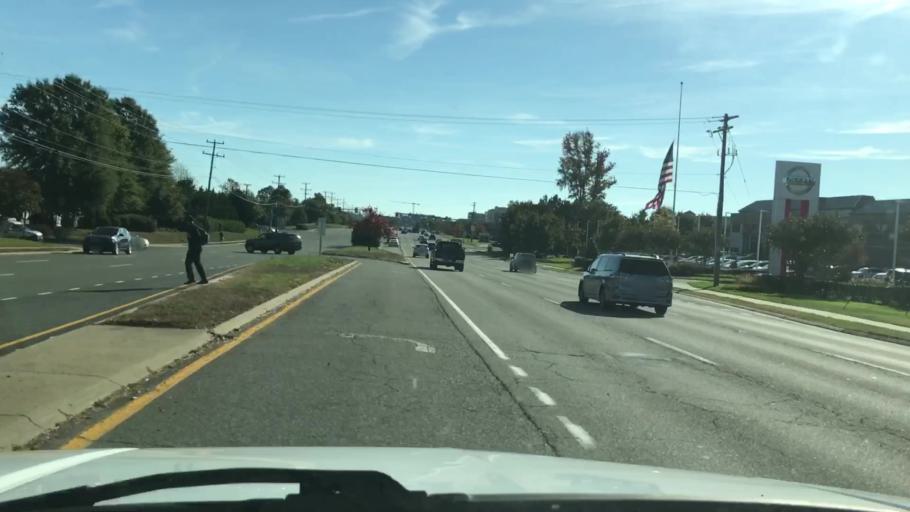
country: US
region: Virginia
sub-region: Henrico County
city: Short Pump
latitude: 37.6510
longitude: -77.6100
